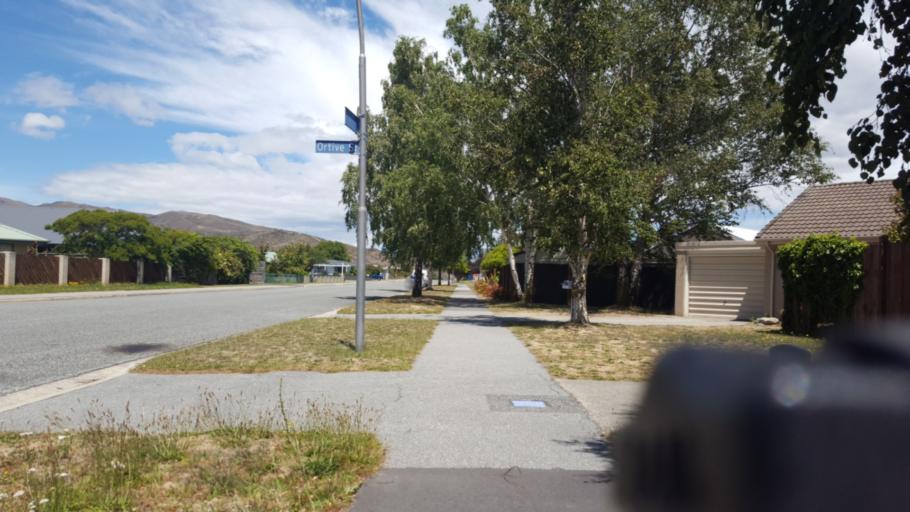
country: NZ
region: Otago
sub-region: Queenstown-Lakes District
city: Wanaka
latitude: -45.0425
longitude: 169.2055
